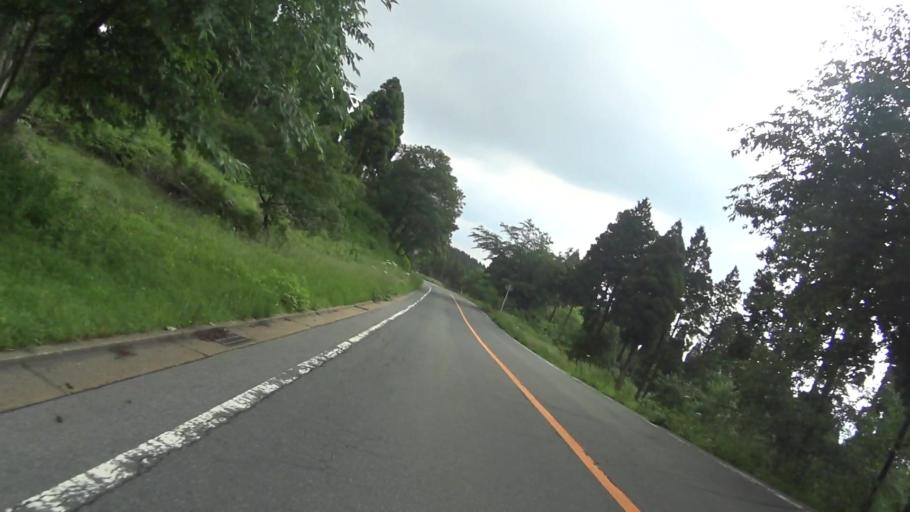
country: JP
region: Kumamoto
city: Aso
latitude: 32.8922
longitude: 131.0504
